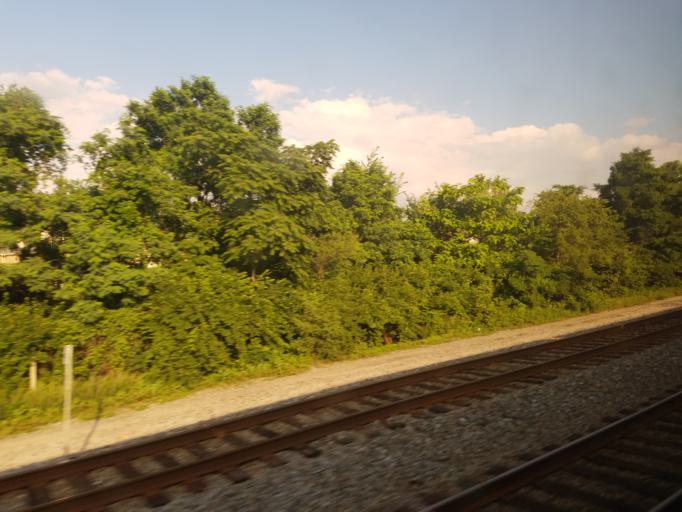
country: US
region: Virginia
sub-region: City of Alexandria
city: Alexandria
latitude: 38.8279
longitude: -77.0470
